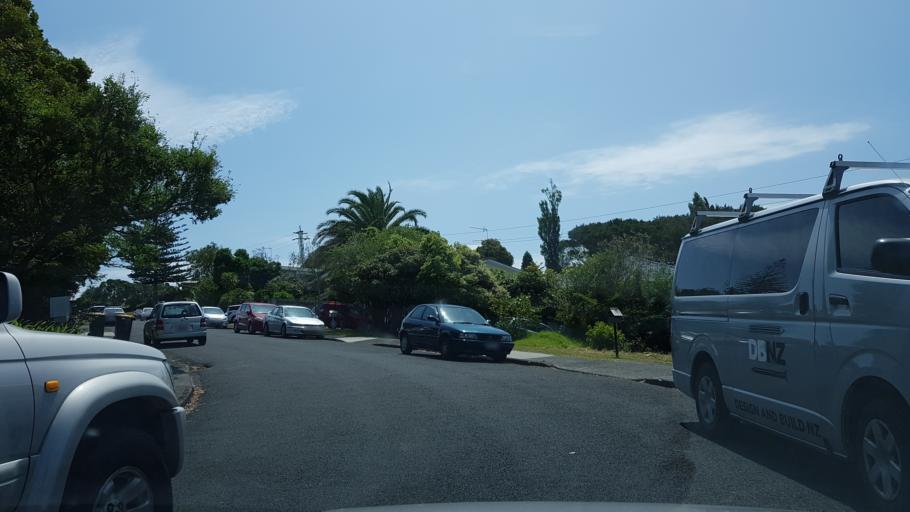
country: NZ
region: Auckland
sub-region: Auckland
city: North Shore
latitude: -36.7807
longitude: 174.7252
